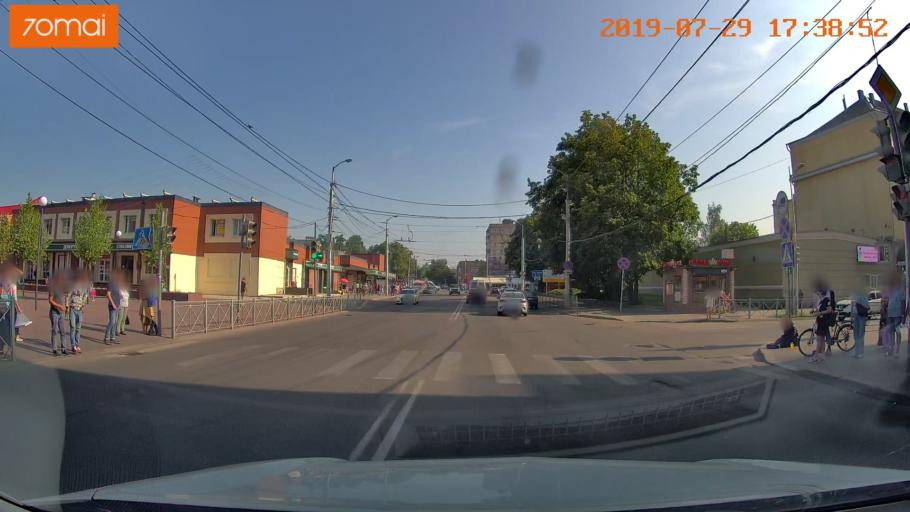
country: RU
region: Kaliningrad
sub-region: Gorod Kaliningrad
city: Kaliningrad
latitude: 54.7210
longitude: 20.5074
